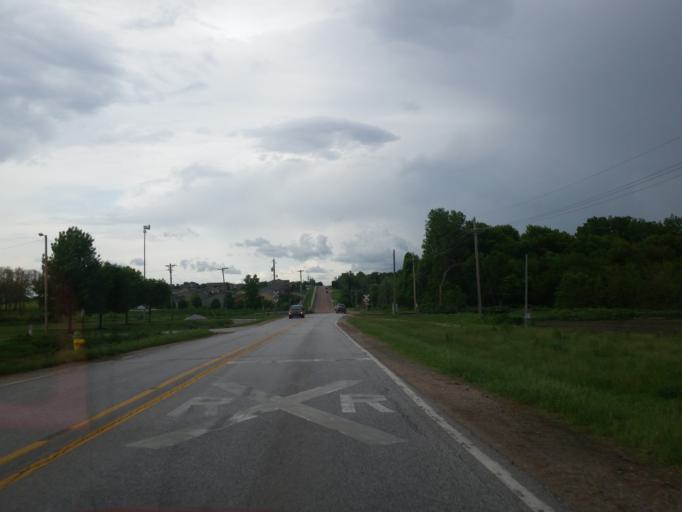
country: US
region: Nebraska
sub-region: Sarpy County
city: Offutt Air Force Base
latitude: 41.1462
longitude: -95.9476
